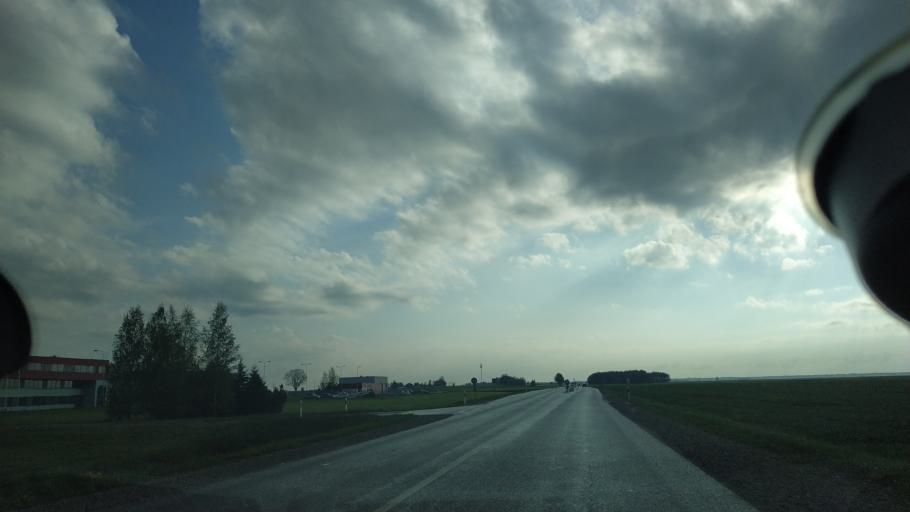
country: LT
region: Kauno apskritis
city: Kedainiai
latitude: 55.2642
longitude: 23.8960
